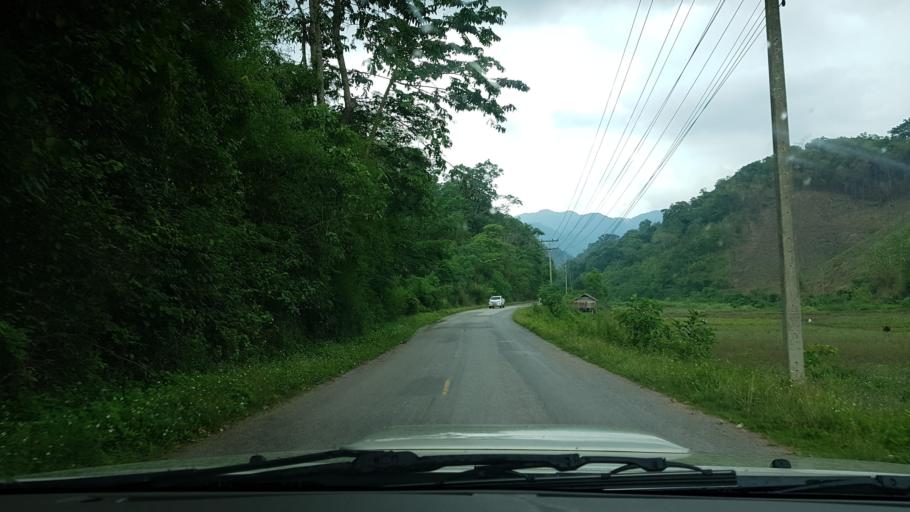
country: LA
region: Oudomxai
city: Muang Xay
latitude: 20.6174
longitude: 101.9534
